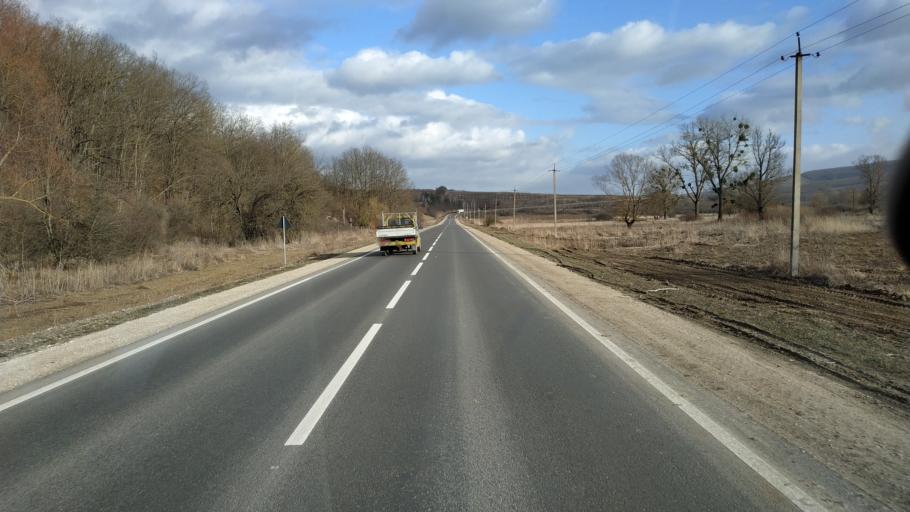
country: MD
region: Calarasi
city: Calarasi
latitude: 47.3021
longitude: 28.1428
